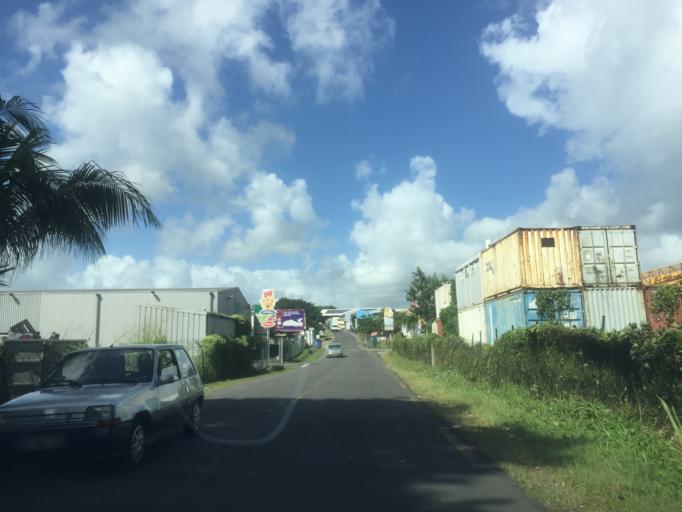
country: GP
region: Guadeloupe
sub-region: Guadeloupe
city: Baie-Mahault
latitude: 16.2409
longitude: -61.5789
